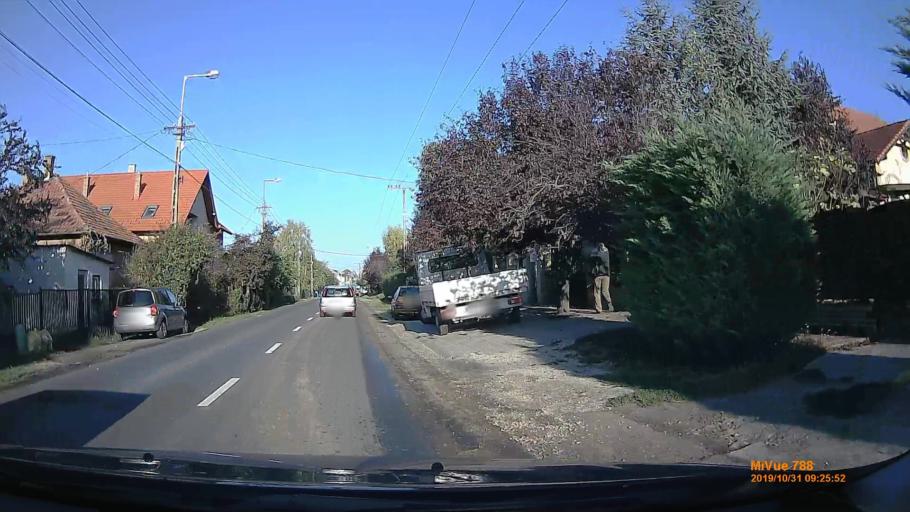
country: HU
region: Pest
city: Maglod
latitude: 47.4449
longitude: 19.3669
